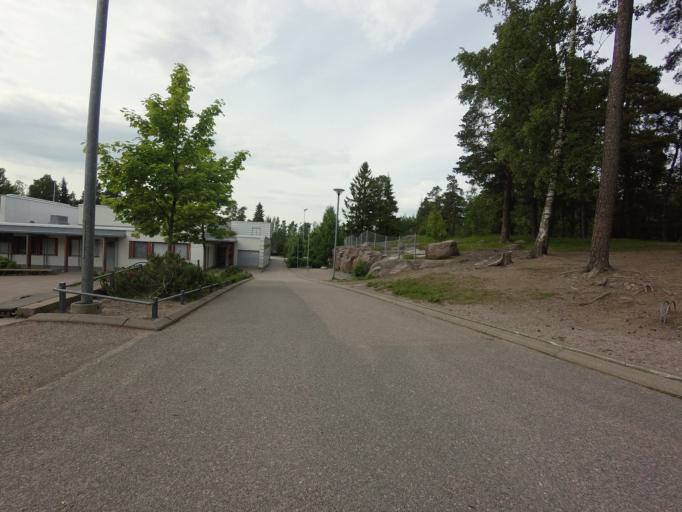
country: FI
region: Uusimaa
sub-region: Helsinki
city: Koukkuniemi
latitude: 60.1550
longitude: 24.7548
